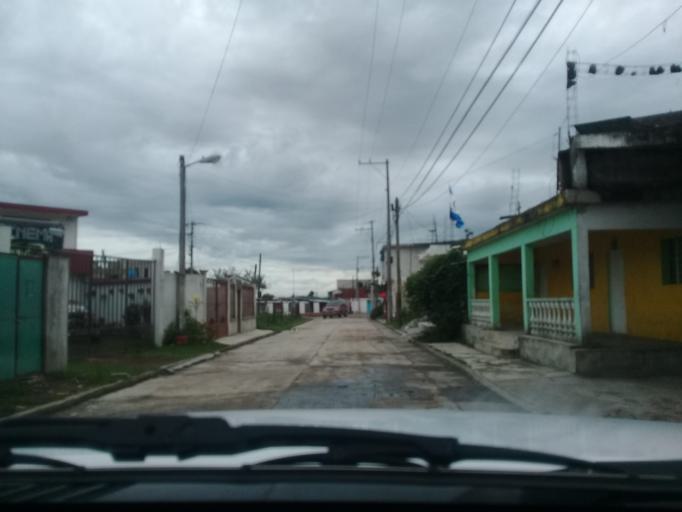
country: MX
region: Veracruz
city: Rafael Lucio
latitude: 19.5926
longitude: -96.9874
